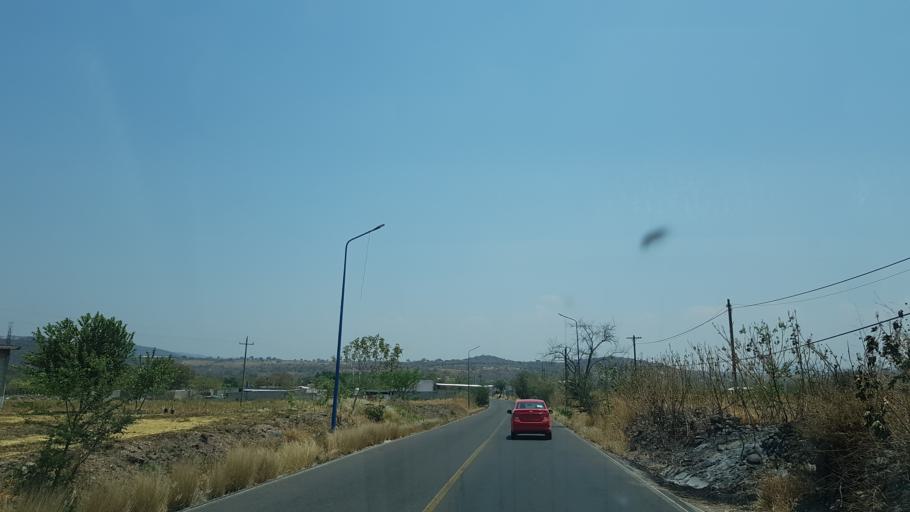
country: MX
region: Puebla
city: Huaquechula
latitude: 18.7648
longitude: -98.5297
